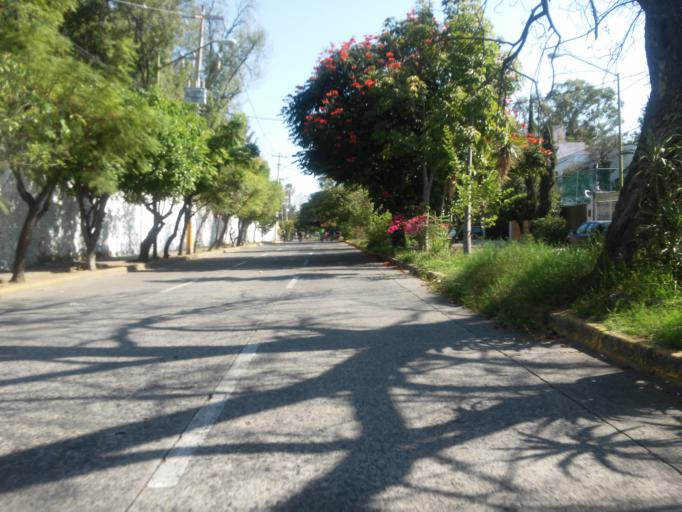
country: MX
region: Jalisco
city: Guadalajara
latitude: 20.6595
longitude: -103.3899
